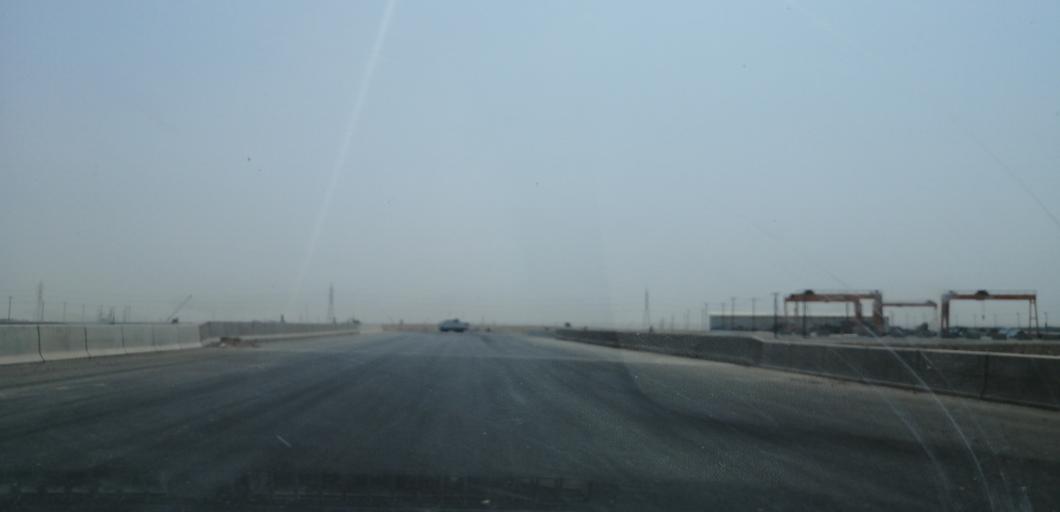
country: KW
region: Muhafazat al Jahra'
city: Al Jahra'
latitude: 29.4462
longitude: 47.6274
